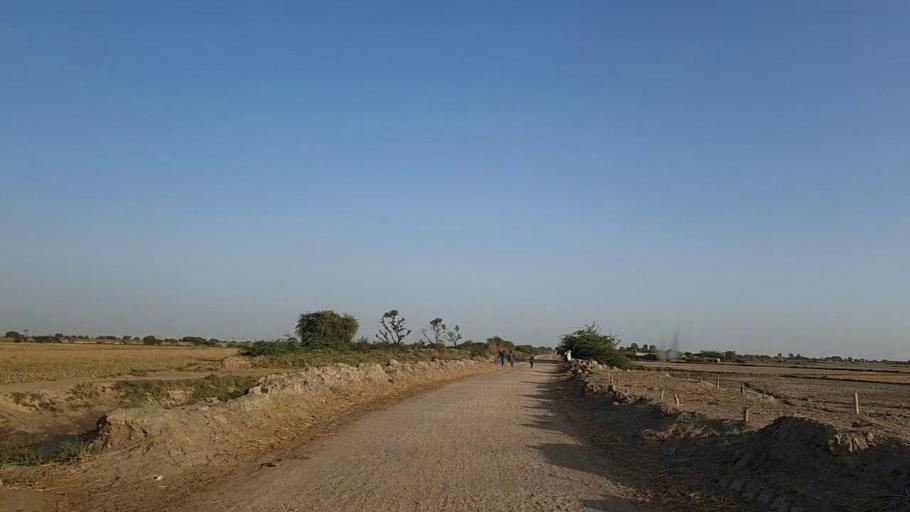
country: PK
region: Sindh
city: Jati
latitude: 24.4154
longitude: 68.3426
